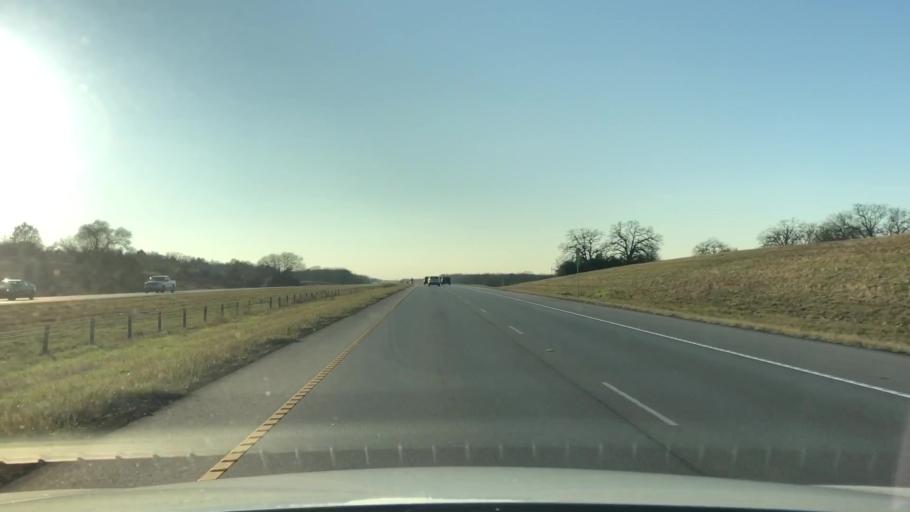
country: US
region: Texas
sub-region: Gonzales County
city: Waelder
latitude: 29.6551
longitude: -97.4477
